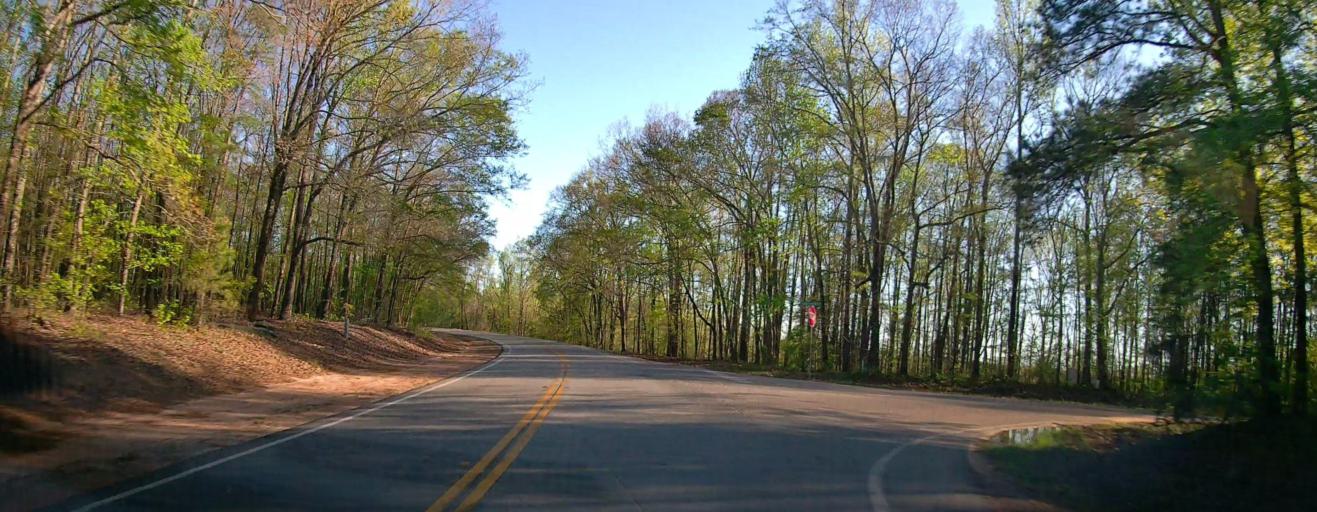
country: US
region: Georgia
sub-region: Wilkinson County
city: Irwinton
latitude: 32.8916
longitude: -83.1337
